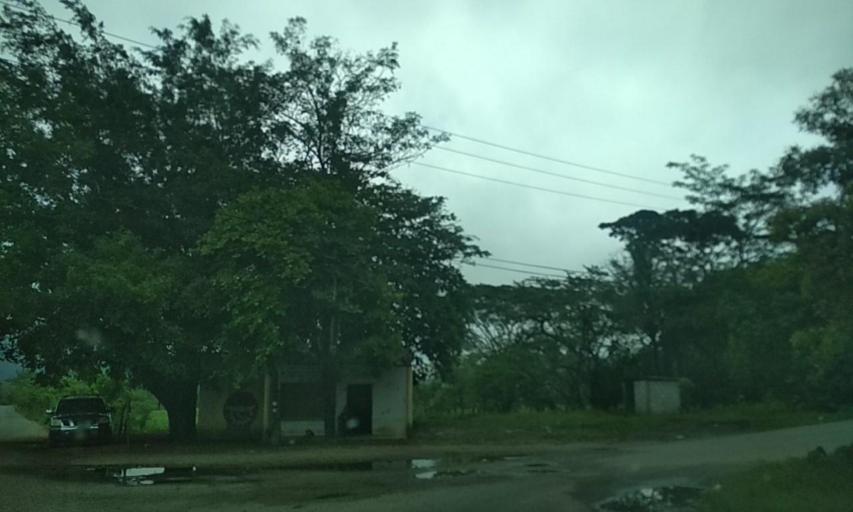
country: MX
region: Veracruz
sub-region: Uxpanapa
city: Poblado 10
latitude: 17.5045
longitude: -94.1608
